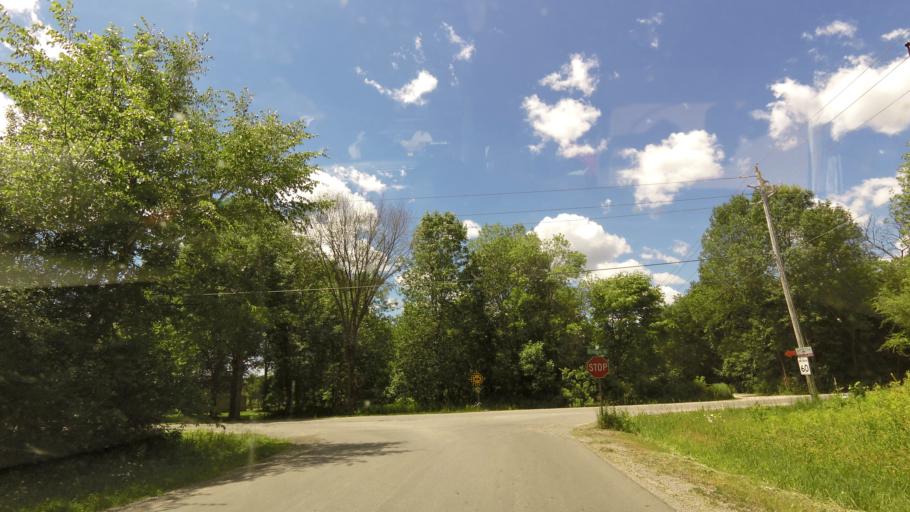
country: CA
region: Ontario
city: Oshawa
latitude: 43.9750
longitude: -78.6270
